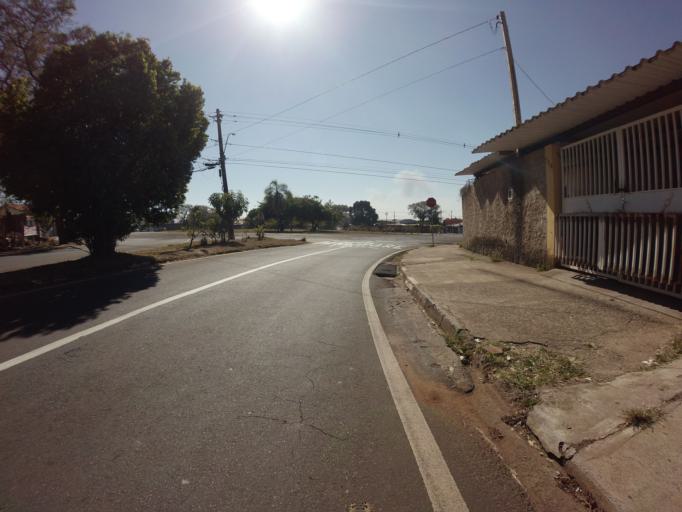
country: BR
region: Sao Paulo
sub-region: Piracicaba
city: Piracicaba
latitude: -22.7690
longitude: -47.5870
